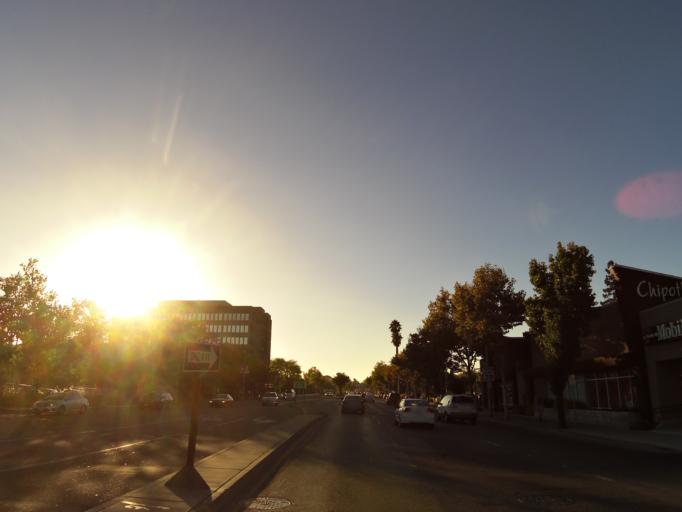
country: US
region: California
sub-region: Santa Clara County
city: Palo Alto
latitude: 37.4235
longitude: -122.1428
